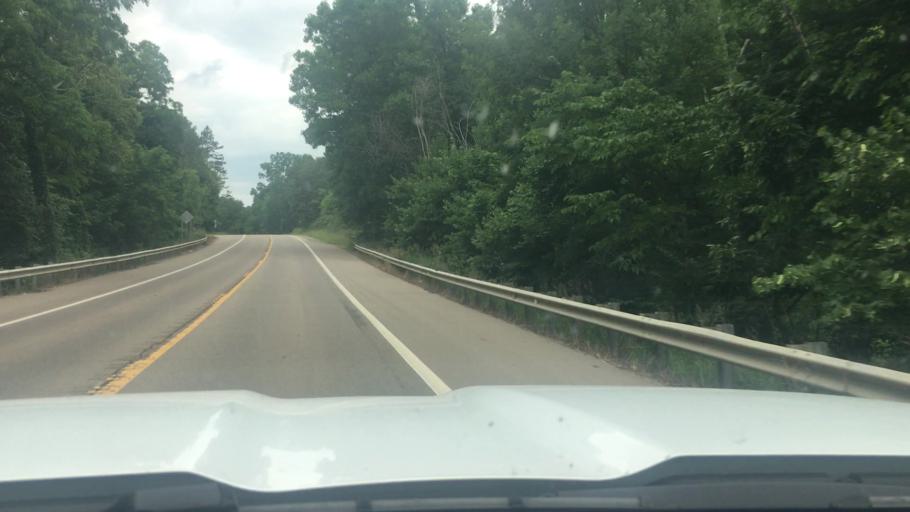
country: US
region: Michigan
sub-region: Ionia County
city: Portland
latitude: 43.0010
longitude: -84.9225
